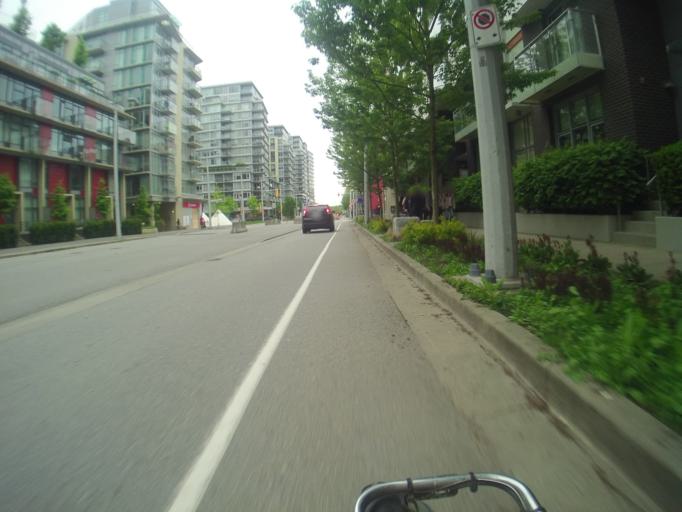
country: CA
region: British Columbia
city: Vancouver
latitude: 49.2703
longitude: -123.1051
